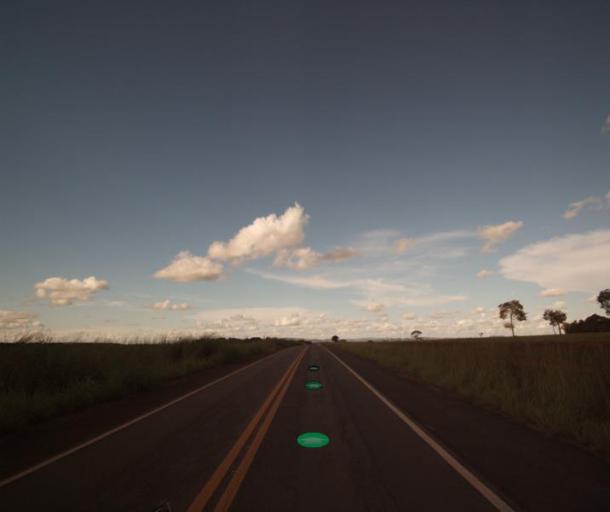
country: BR
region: Goias
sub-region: Itaberai
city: Itaberai
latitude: -15.9666
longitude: -49.6663
